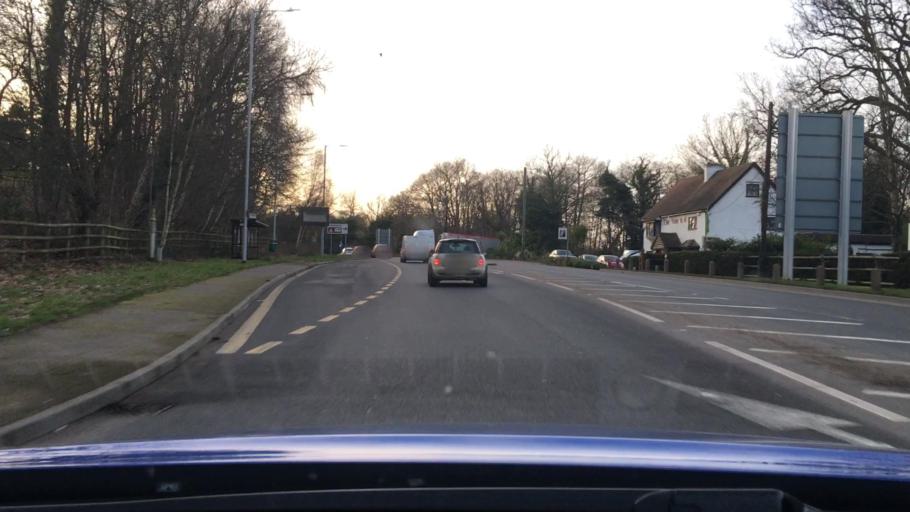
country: GB
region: England
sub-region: Kent
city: Borough Green
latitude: 51.2980
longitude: 0.3470
